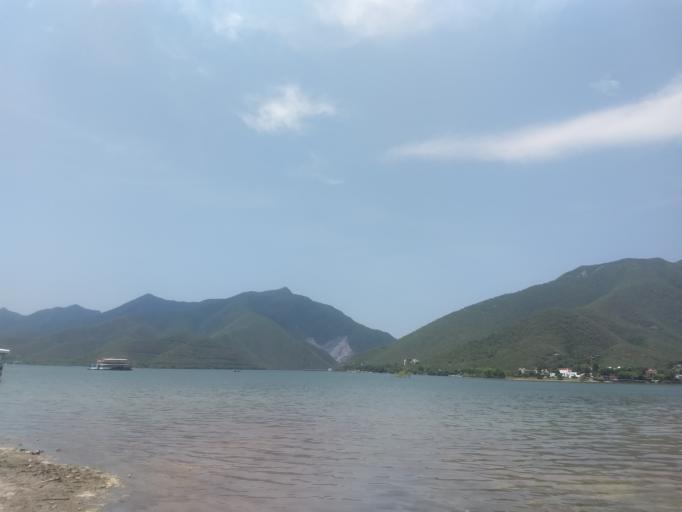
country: MX
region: Nuevo Leon
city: Santiago
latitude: 25.4109
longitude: -100.1372
